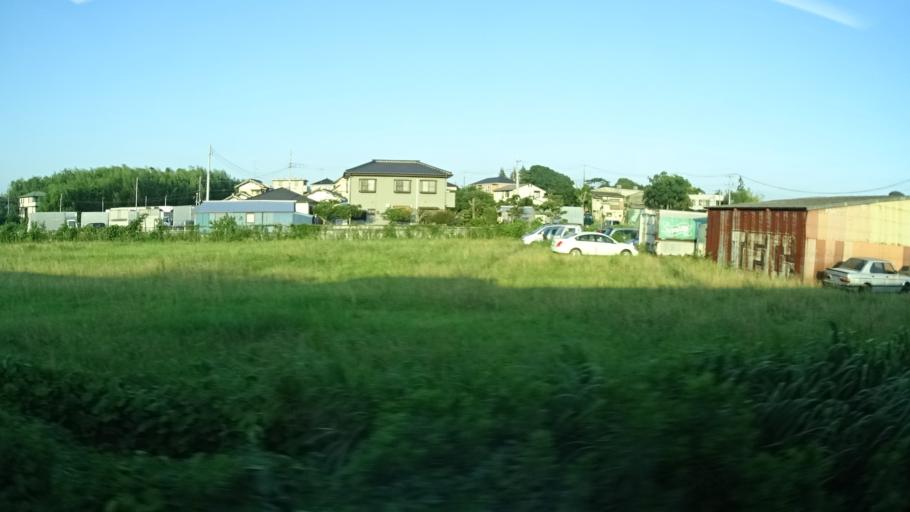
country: JP
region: Ibaraki
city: Ishioka
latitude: 36.1975
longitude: 140.2773
